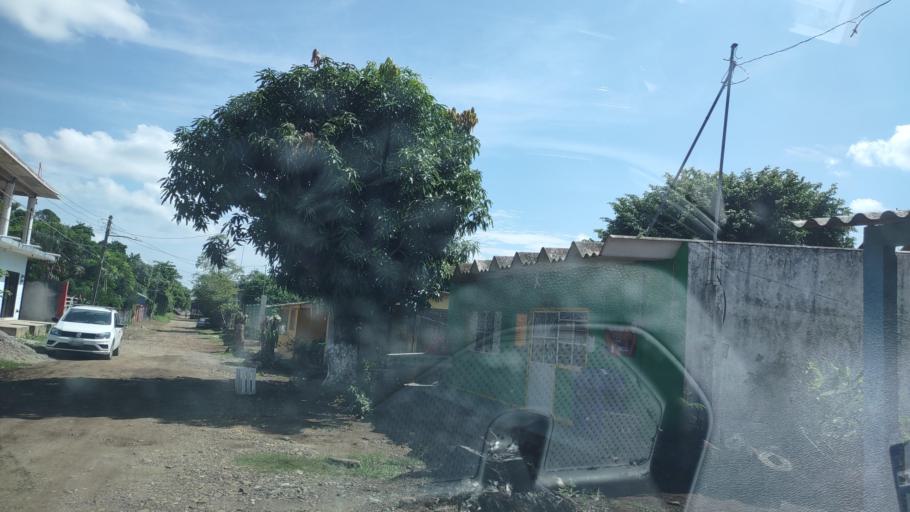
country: MX
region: Veracruz
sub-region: Martinez de la Torre
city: La Union Paso Largo
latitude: 20.1301
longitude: -96.9983
